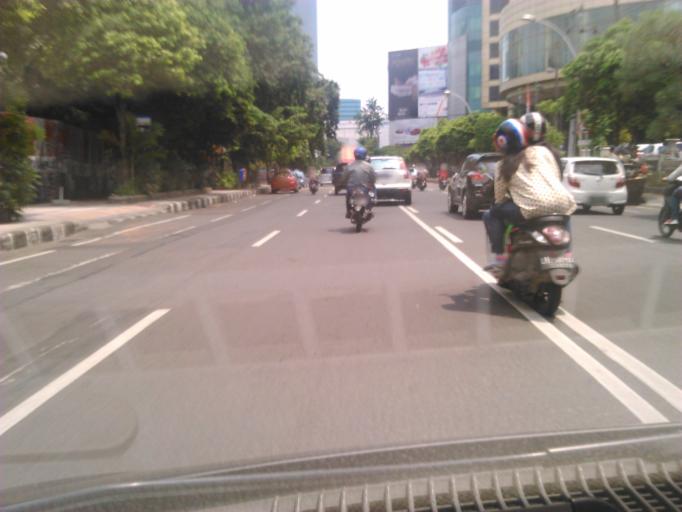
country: ID
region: East Java
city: Gubengairlangga
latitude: -7.2685
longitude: 112.7414
